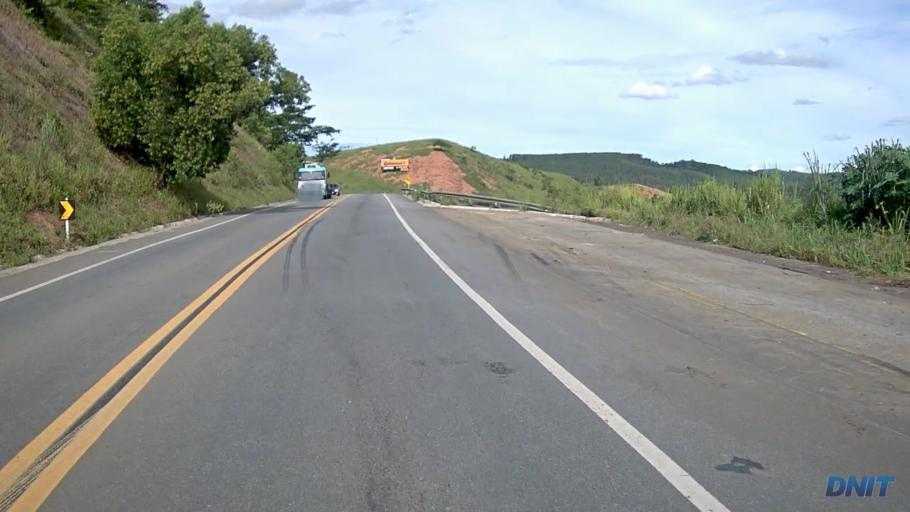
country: BR
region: Minas Gerais
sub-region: Belo Oriente
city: Belo Oriente
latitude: -19.2650
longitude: -42.3505
